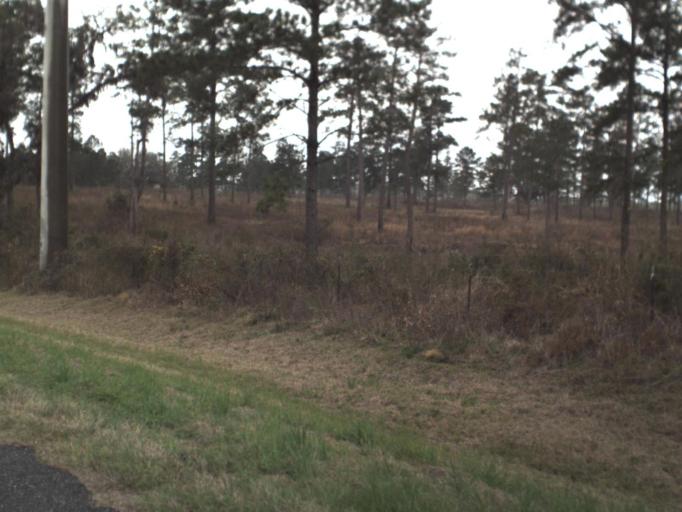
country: US
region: Florida
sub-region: Jefferson County
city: Monticello
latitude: 30.4058
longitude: -84.0087
